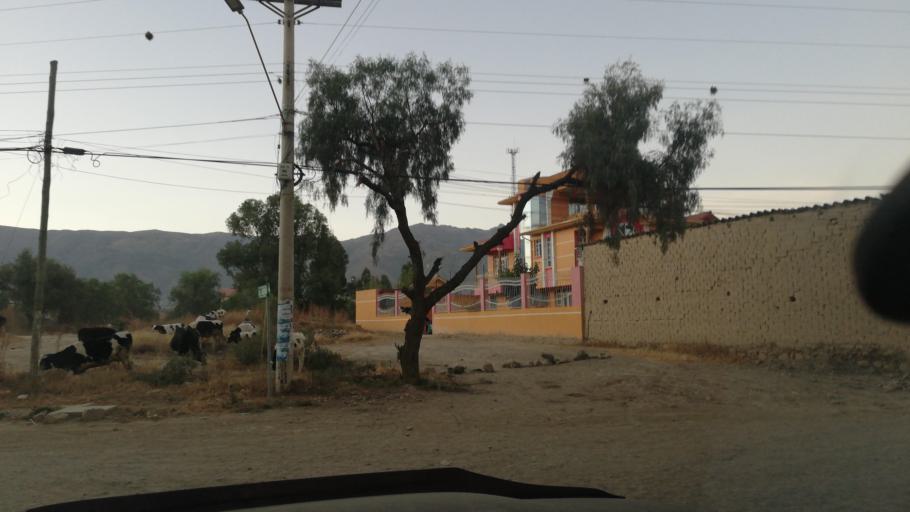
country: BO
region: Cochabamba
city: Cochabamba
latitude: -17.3800
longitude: -66.2212
